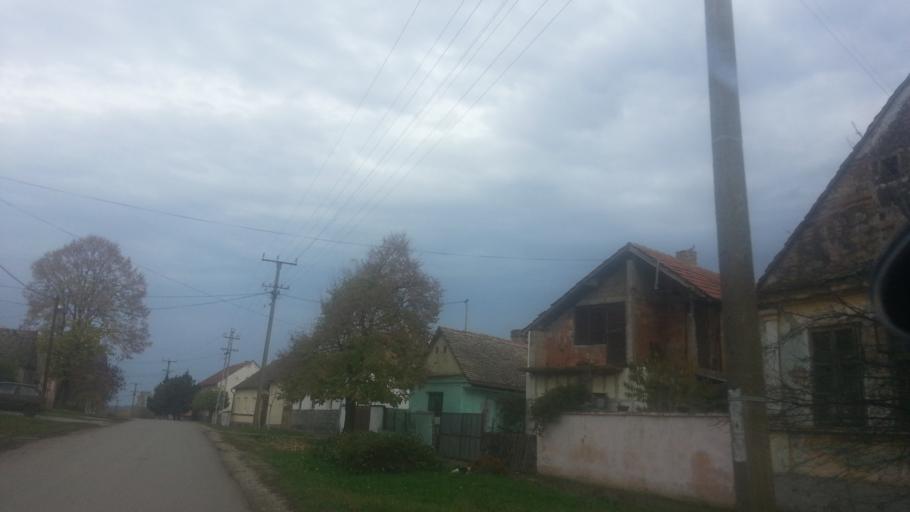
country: RS
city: Putinci
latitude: 44.9933
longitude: 19.9731
